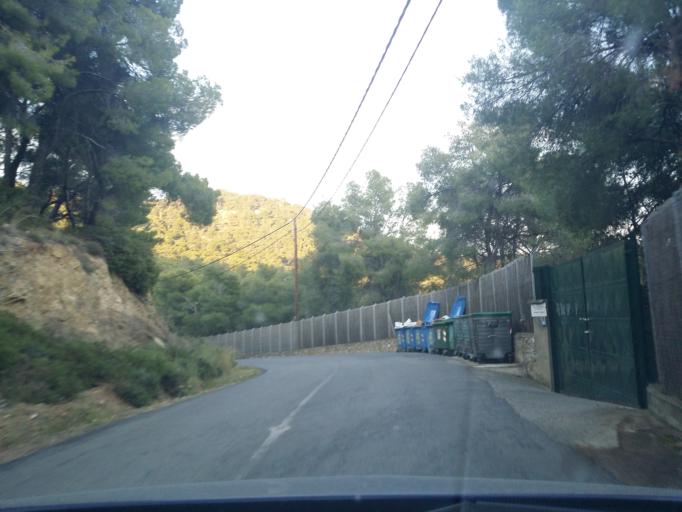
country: GR
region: Attica
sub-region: Nomos Piraios
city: Poros
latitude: 37.5064
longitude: 23.4806
